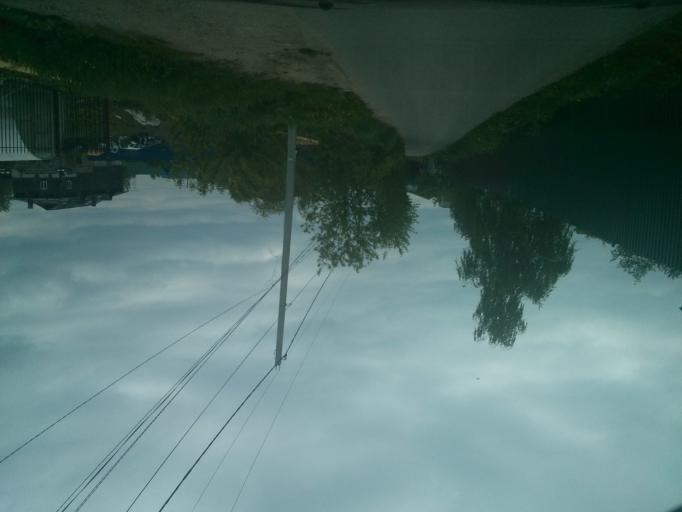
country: RU
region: Nizjnij Novgorod
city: Afonino
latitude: 56.2991
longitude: 44.1000
